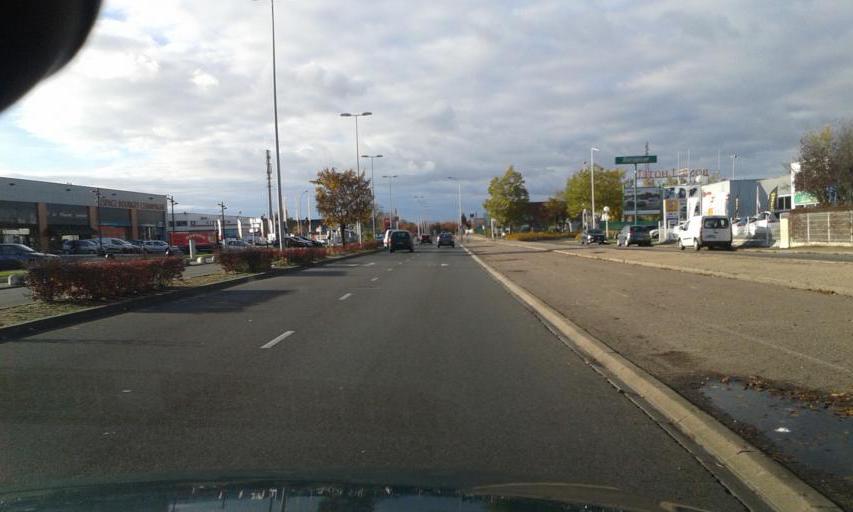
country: FR
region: Centre
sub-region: Departement du Loiret
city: Olivet
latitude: 47.8439
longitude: 1.9220
